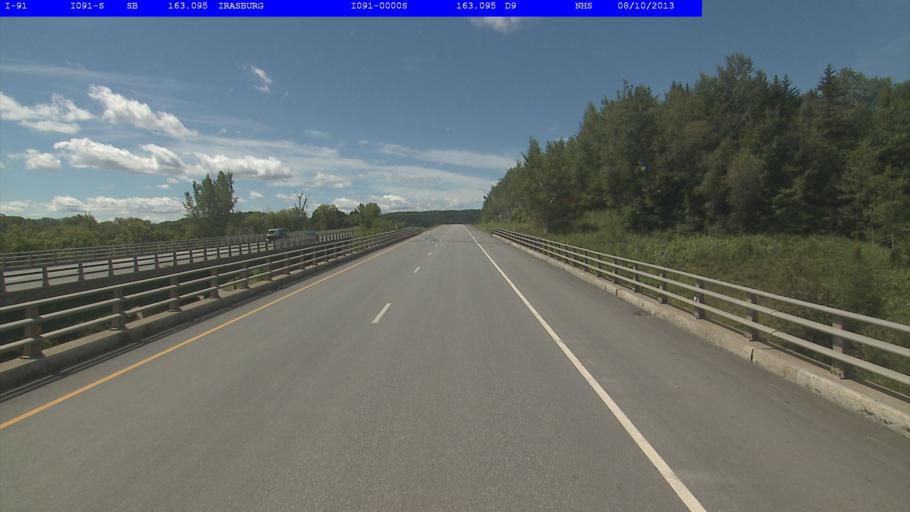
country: US
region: Vermont
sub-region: Orleans County
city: Newport
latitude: 44.8290
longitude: -72.2015
